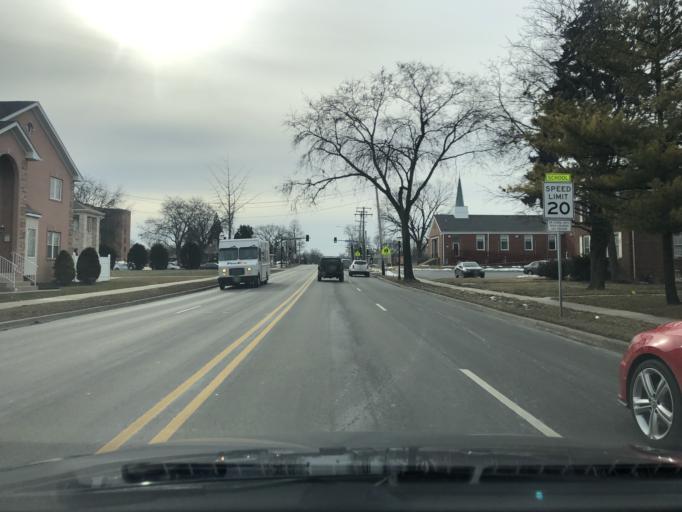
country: US
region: Illinois
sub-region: DuPage County
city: Bensenville
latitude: 41.9514
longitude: -87.9397
